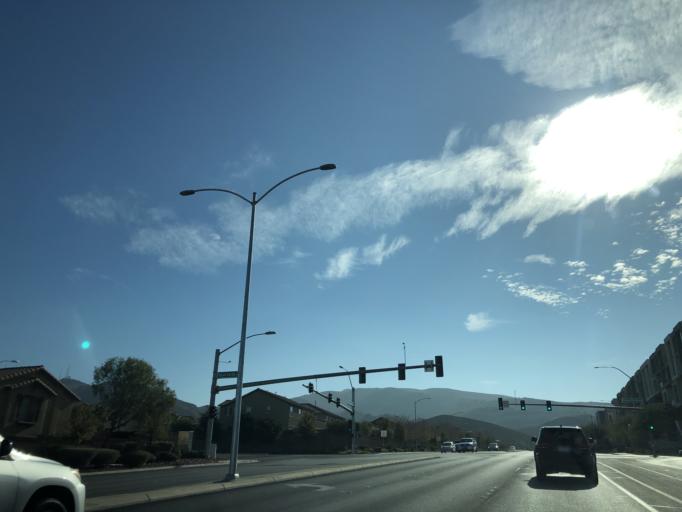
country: US
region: Nevada
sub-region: Clark County
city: Henderson
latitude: 36.0263
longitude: -115.0296
